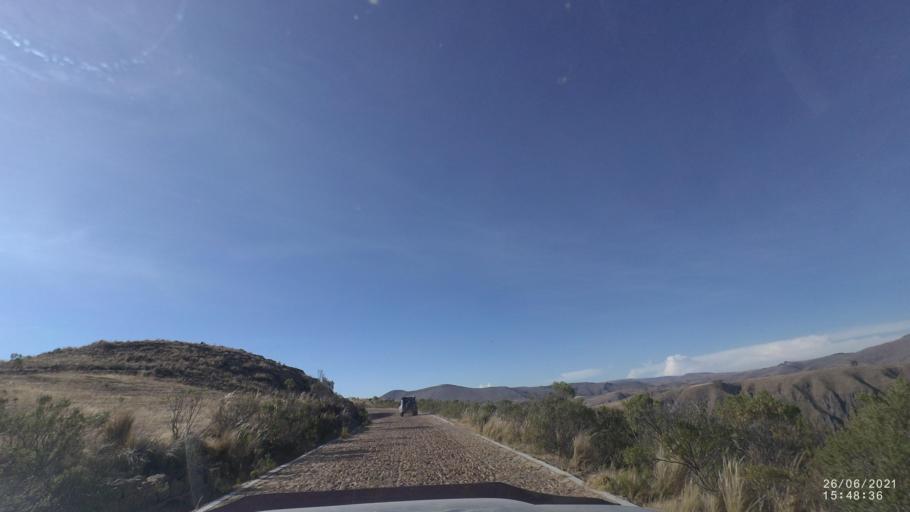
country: BO
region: Cochabamba
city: Arani
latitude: -17.8615
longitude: -65.6955
